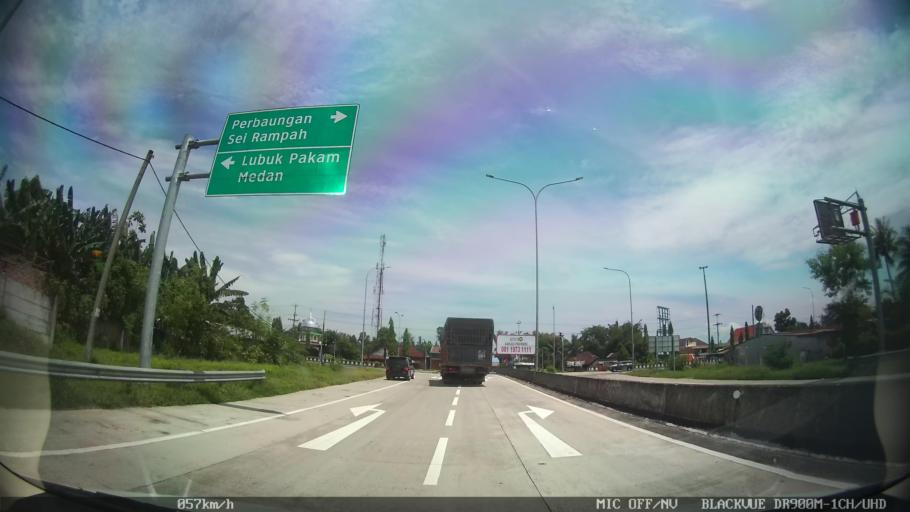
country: ID
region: North Sumatra
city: Perbaungan
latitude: 3.5557
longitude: 98.8862
